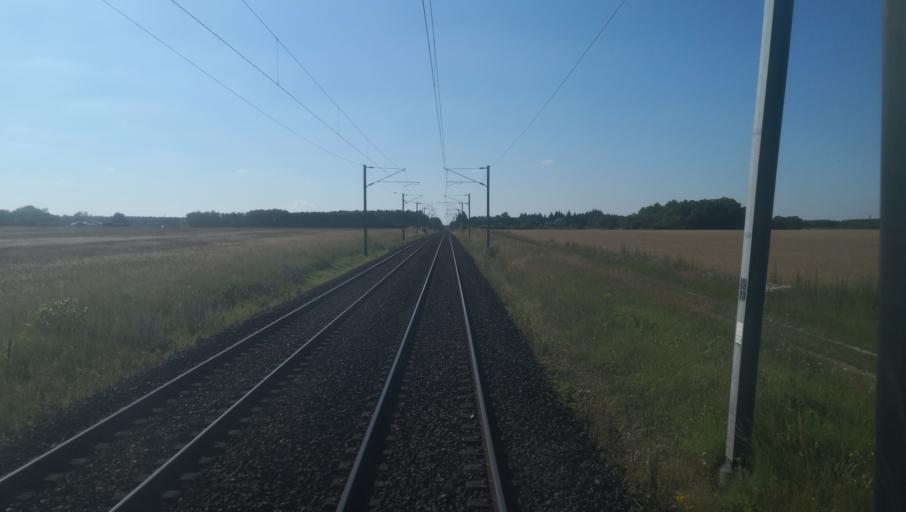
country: FR
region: Centre
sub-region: Departement du Loiret
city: Briare
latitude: 47.5999
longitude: 2.7910
